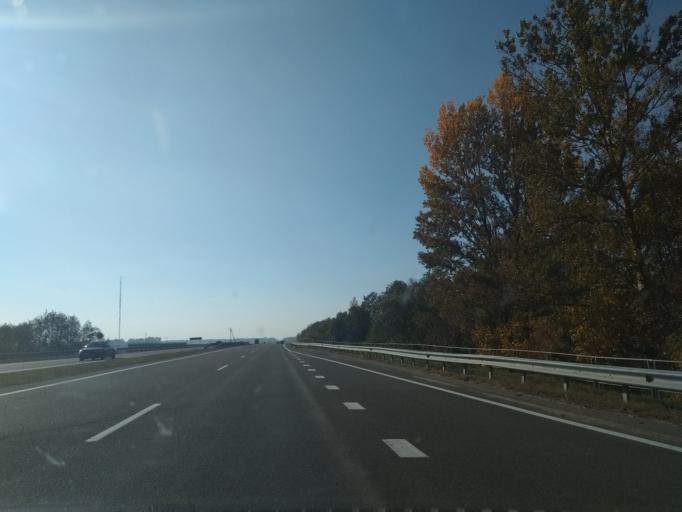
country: BY
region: Brest
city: Zhabinka
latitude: 52.1464
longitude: 24.0041
